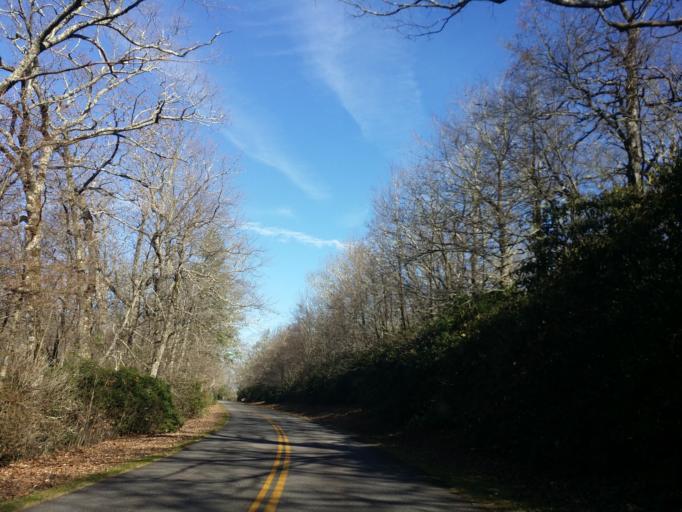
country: US
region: North Carolina
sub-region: Mitchell County
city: Spruce Pine
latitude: 35.7949
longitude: -82.1621
